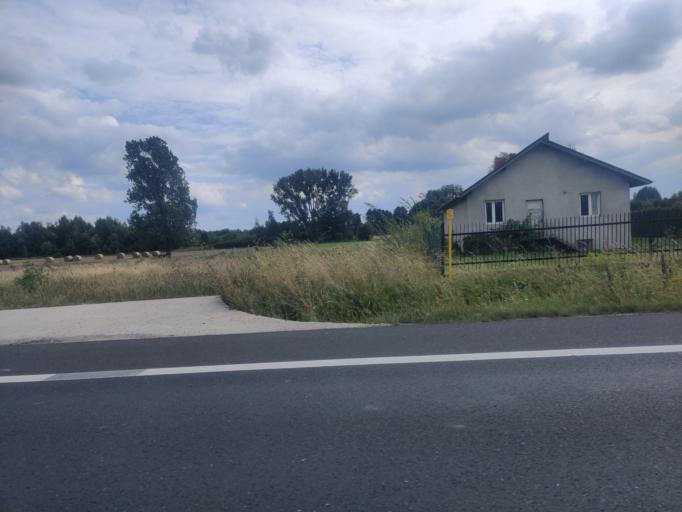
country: PL
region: Greater Poland Voivodeship
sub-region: Powiat koninski
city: Stare Miasto
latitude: 52.1889
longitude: 18.2409
